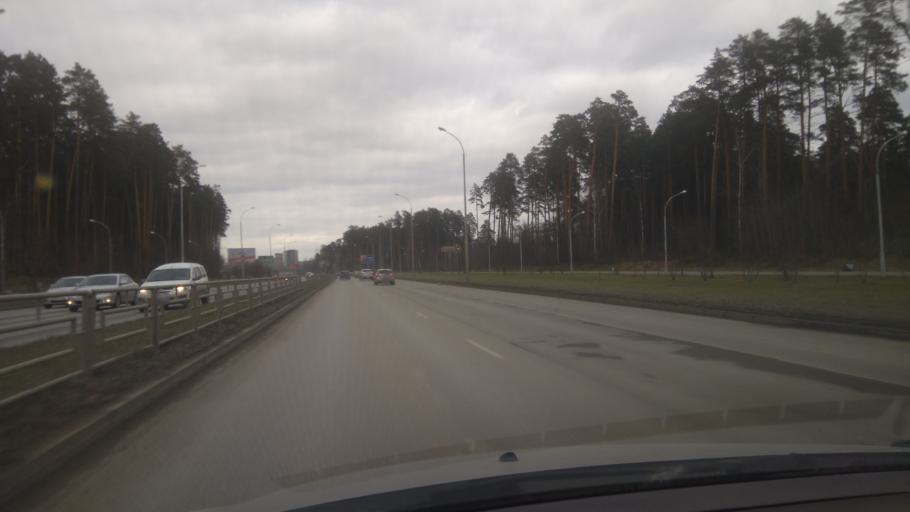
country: RU
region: Sverdlovsk
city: Sovkhoznyy
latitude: 56.7979
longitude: 60.5303
